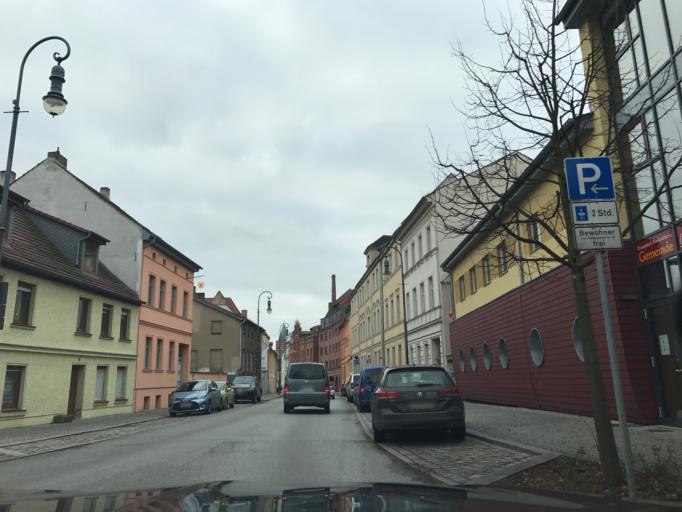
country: DE
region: Brandenburg
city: Brandenburg an der Havel
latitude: 52.4134
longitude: 12.5658
